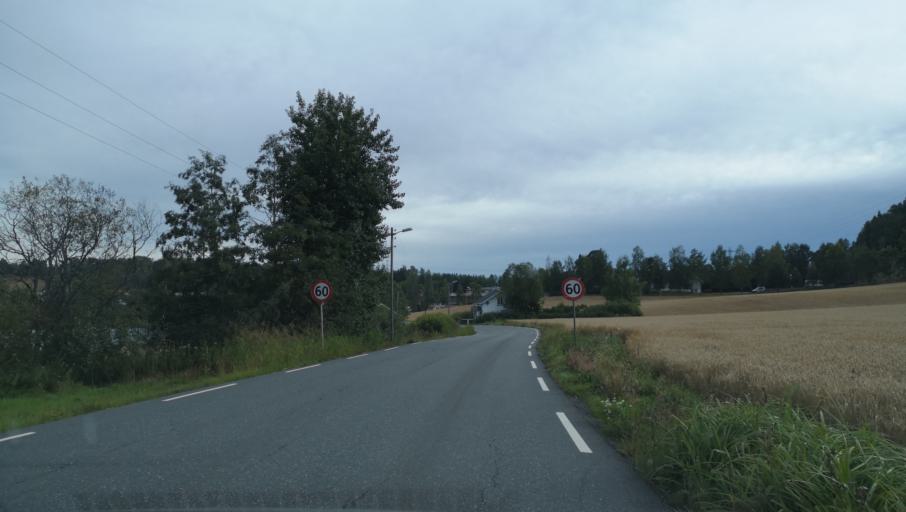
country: NO
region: Ostfold
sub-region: Hobol
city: Tomter
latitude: 59.6892
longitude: 11.0381
